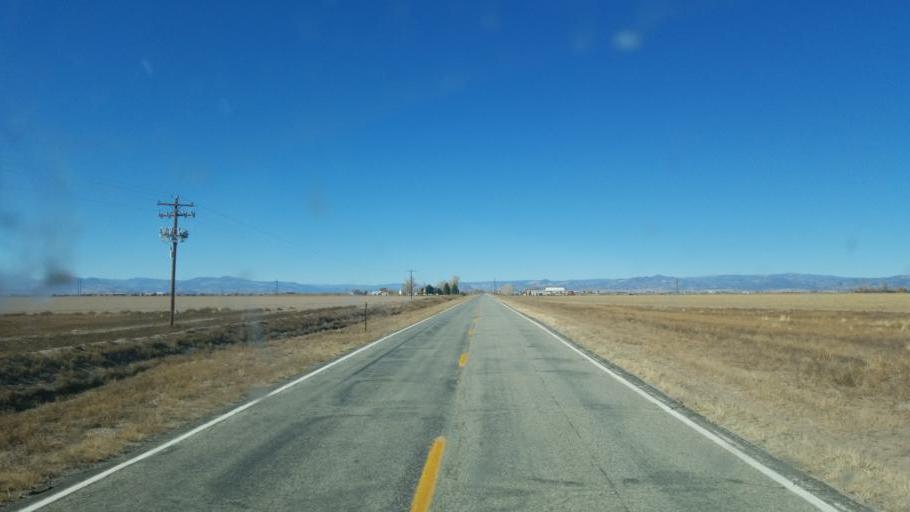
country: US
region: Colorado
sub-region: Saguache County
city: Center
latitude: 37.7485
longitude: -106.0204
